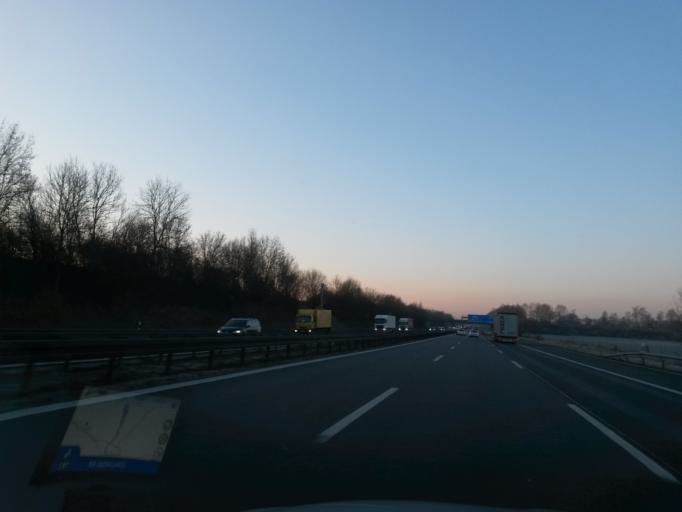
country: DE
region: Bavaria
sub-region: Upper Bavaria
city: Allershausen
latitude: 48.4390
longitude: 11.5892
